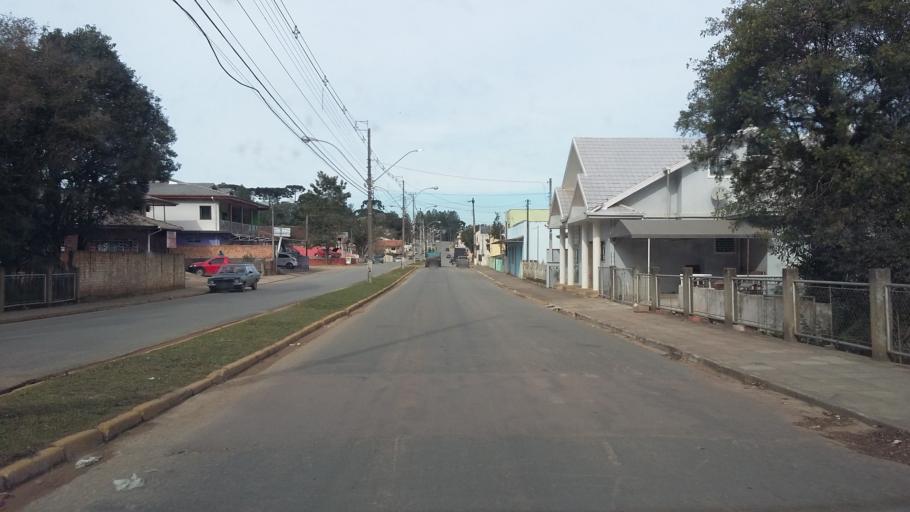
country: BR
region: Parana
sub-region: Lapa
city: Lapa
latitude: -25.8765
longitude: -49.4967
